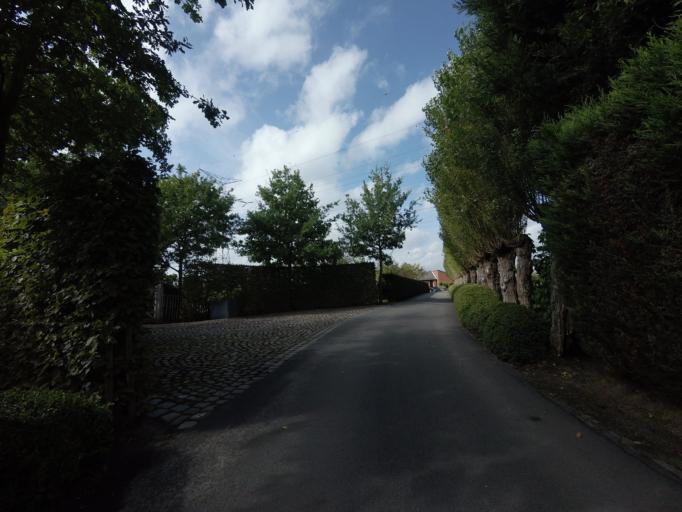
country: BE
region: Flanders
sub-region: Provincie Antwerpen
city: Aartselaar
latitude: 51.1138
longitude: 4.3882
